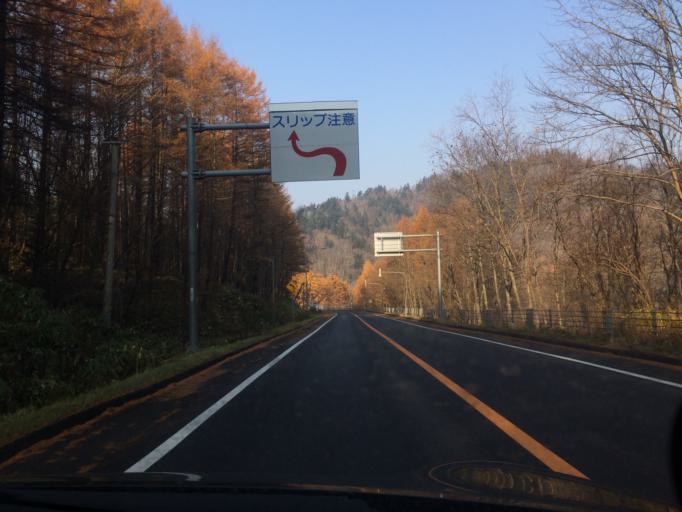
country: JP
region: Hokkaido
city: Iwamizawa
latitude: 42.9294
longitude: 142.1128
